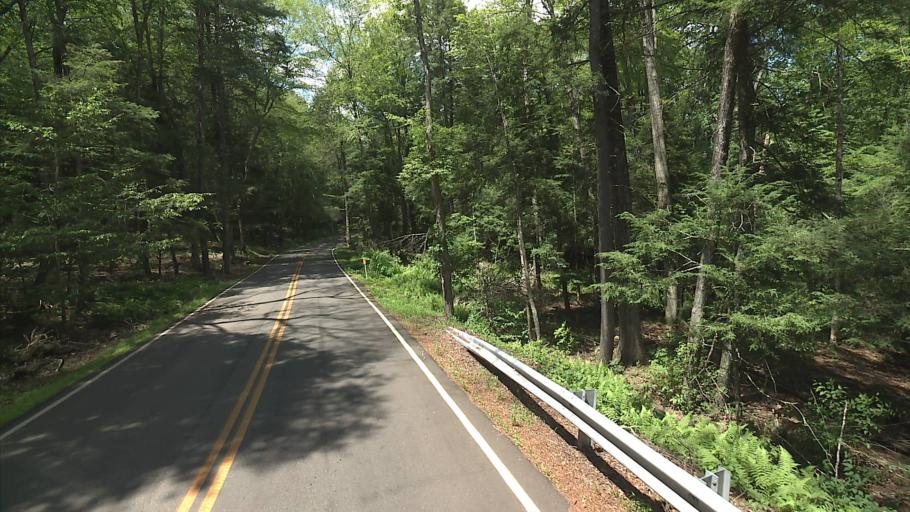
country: US
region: Connecticut
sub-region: New London County
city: Colchester
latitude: 41.4618
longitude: -72.3359
